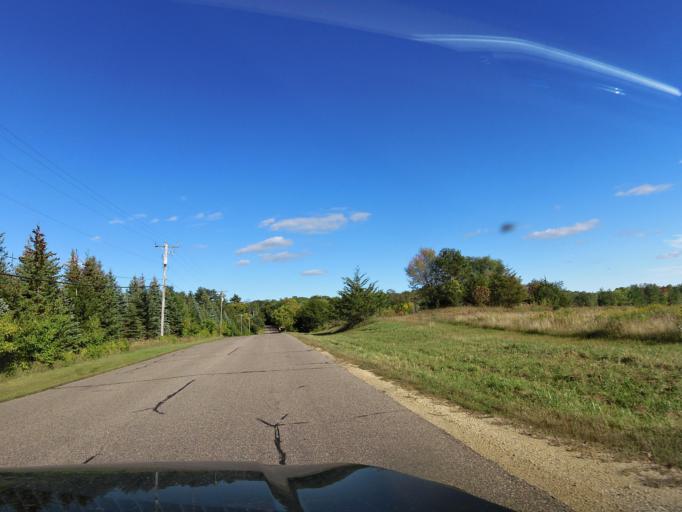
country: US
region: Minnesota
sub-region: Washington County
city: Afton
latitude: 44.8764
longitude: -92.8106
